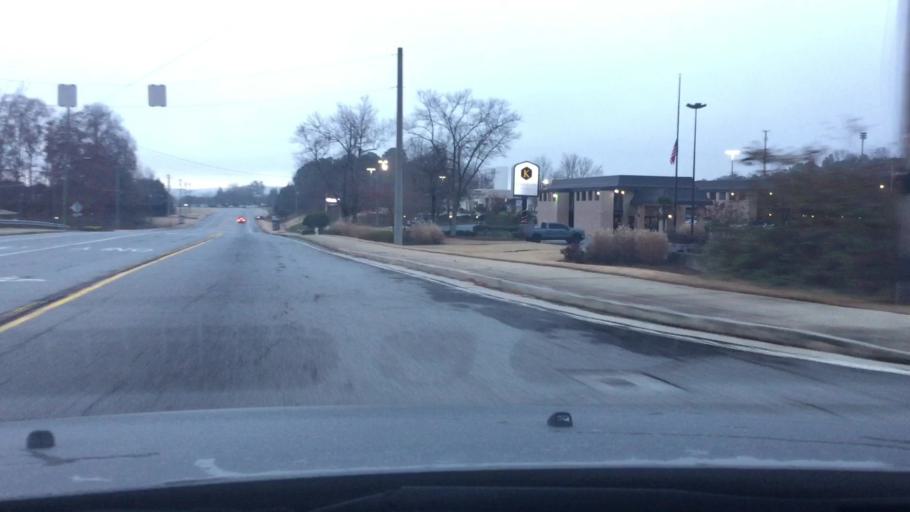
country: US
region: Georgia
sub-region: Cobb County
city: Kennesaw
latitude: 34.0335
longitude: -84.5742
